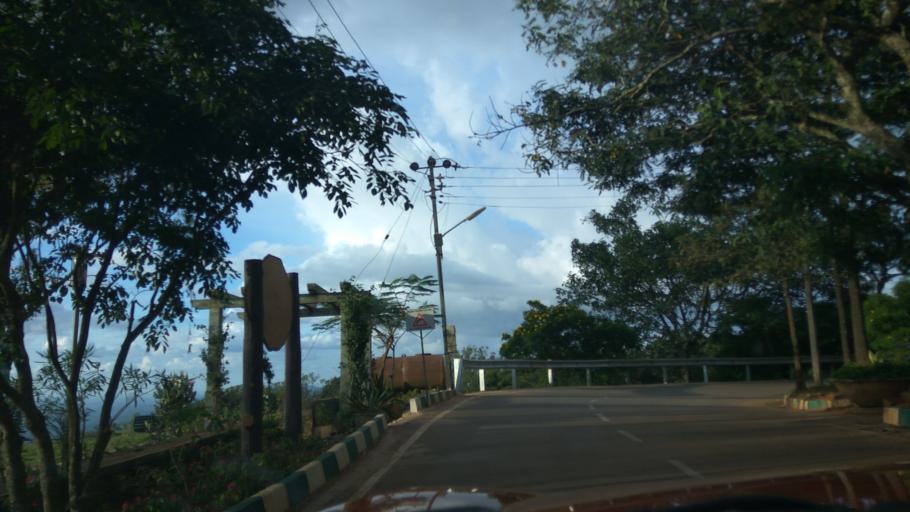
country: IN
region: Karnataka
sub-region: Chikkaballapur
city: Chik Ballapur
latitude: 13.3697
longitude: 77.6821
